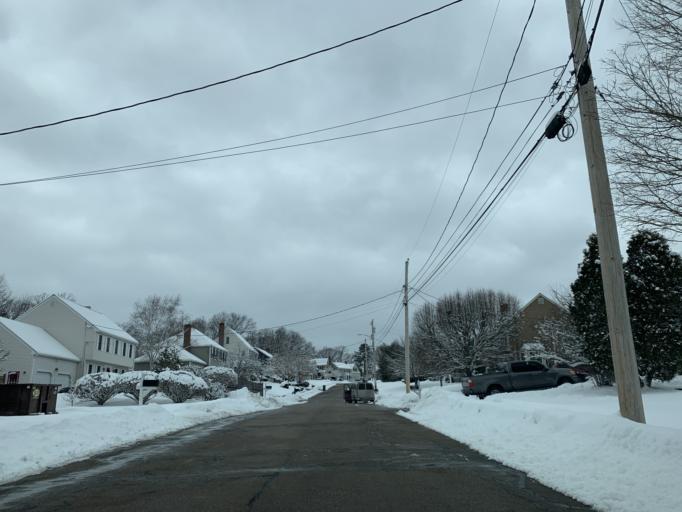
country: US
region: Massachusetts
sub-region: Norfolk County
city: Norwood
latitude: 42.1702
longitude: -71.1766
